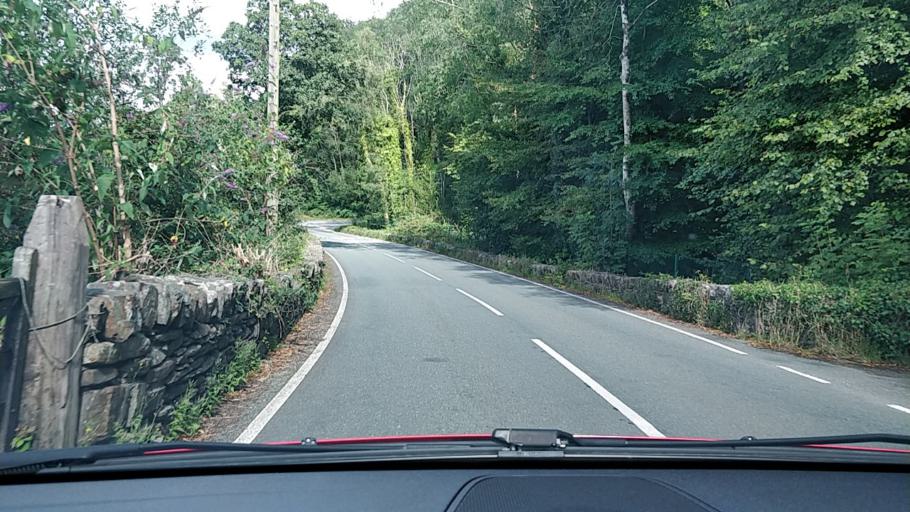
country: GB
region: Wales
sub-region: Gwynedd
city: Maentwrog
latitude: 52.9366
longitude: -4.0049
